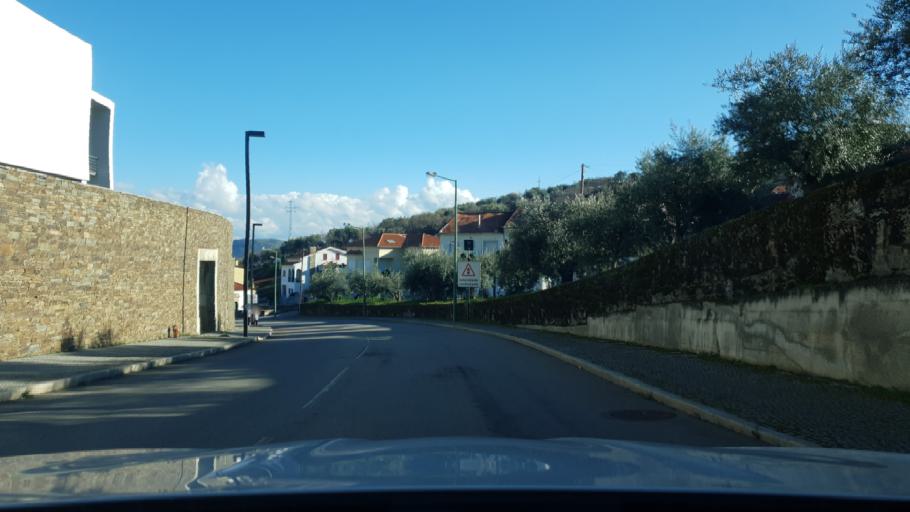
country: PT
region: Braganca
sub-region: Freixo de Espada A Cinta
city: Freixo de Espada a Cinta
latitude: 41.0944
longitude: -6.8132
